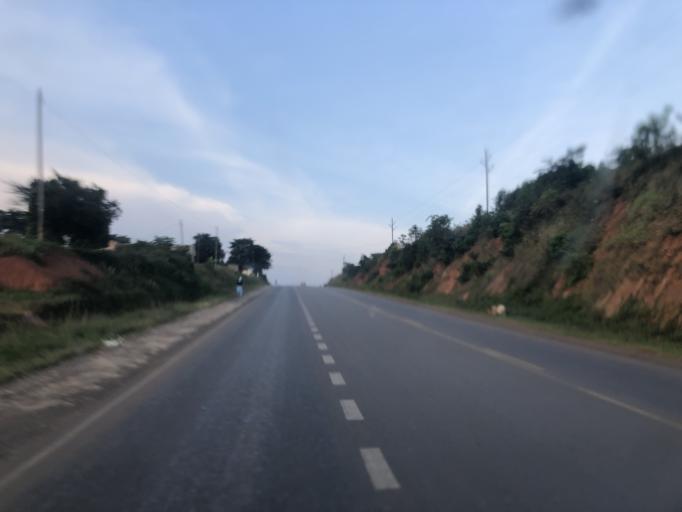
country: UG
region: Central Region
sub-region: Mpigi District
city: Mpigi
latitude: 0.2168
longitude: 32.3297
